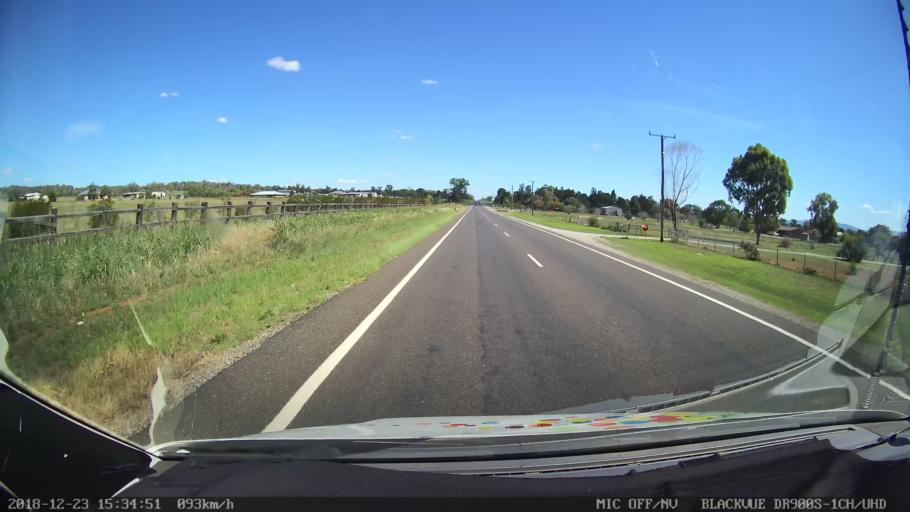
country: AU
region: New South Wales
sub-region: Tamworth Municipality
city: Tamworth
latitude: -31.0194
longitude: 150.8801
